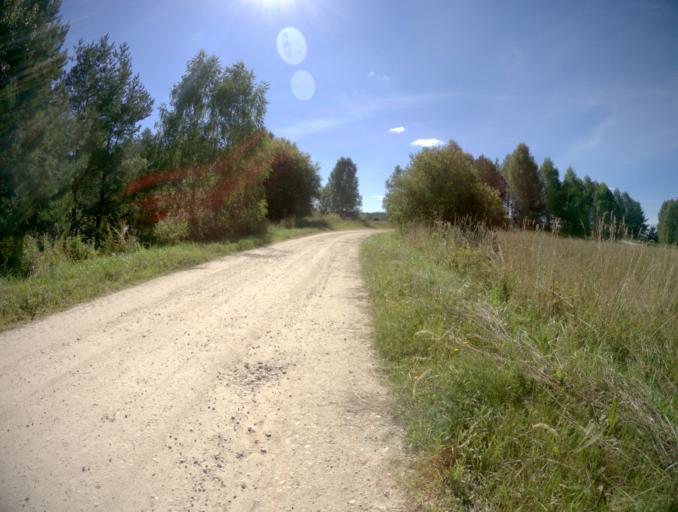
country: RU
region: Vladimir
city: Dobryatino
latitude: 55.6403
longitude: 41.2736
